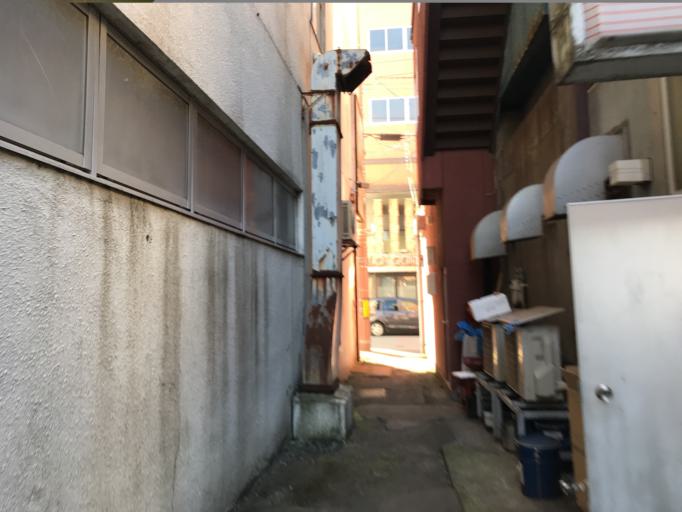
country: JP
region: Hokkaido
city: Muroran
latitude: 42.3176
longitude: 140.9723
